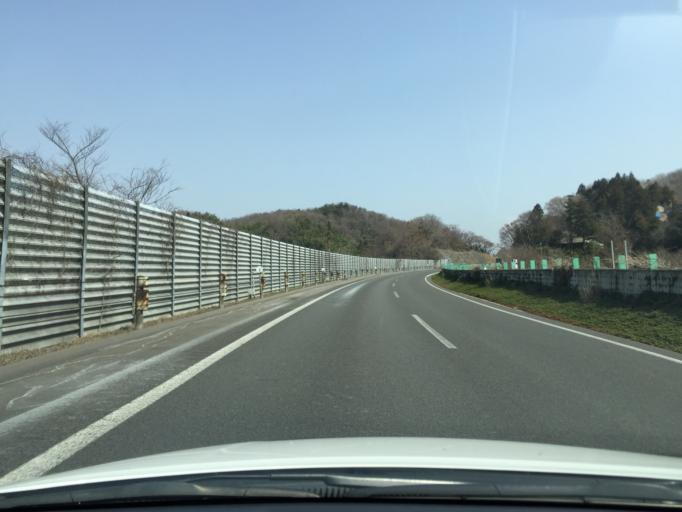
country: JP
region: Miyagi
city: Shiroishi
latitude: 37.9346
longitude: 140.6088
